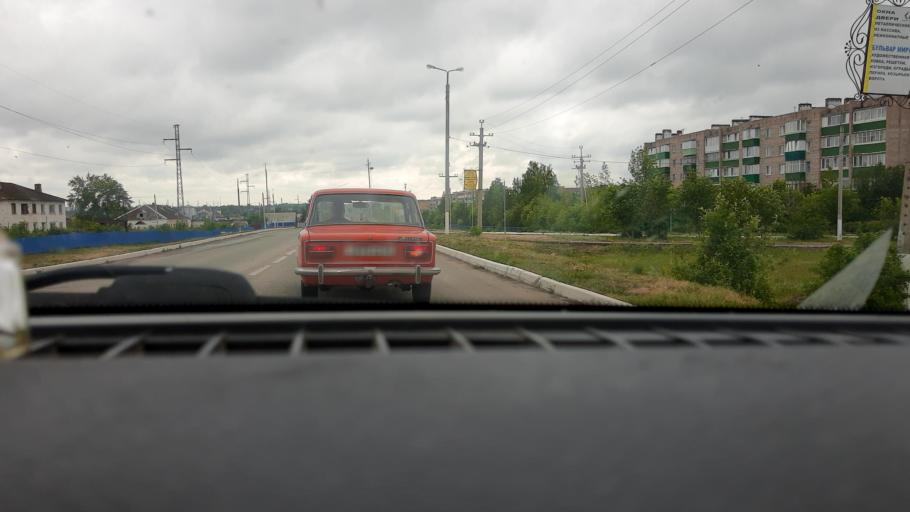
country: RU
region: Bashkortostan
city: Priyutovo
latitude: 53.9042
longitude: 53.9402
